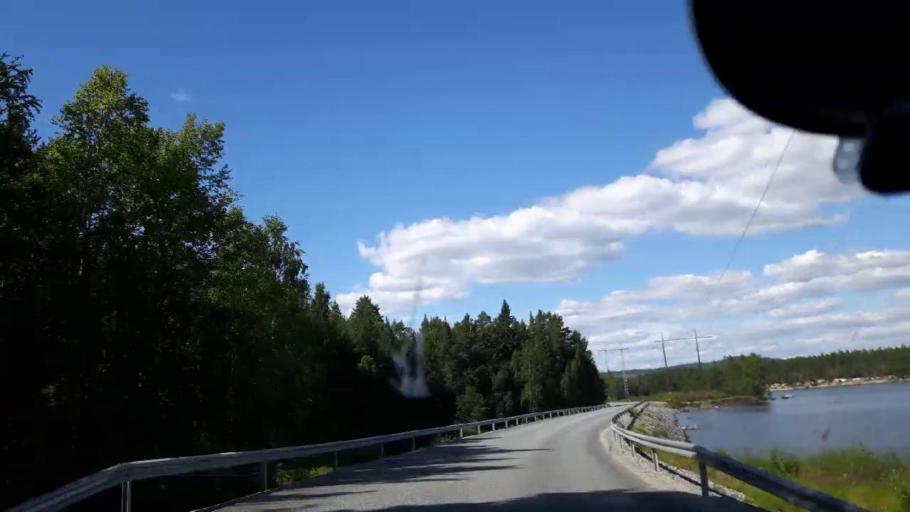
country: SE
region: Vaesternorrland
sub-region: Ange Kommun
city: Fransta
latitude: 62.6896
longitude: 16.3966
